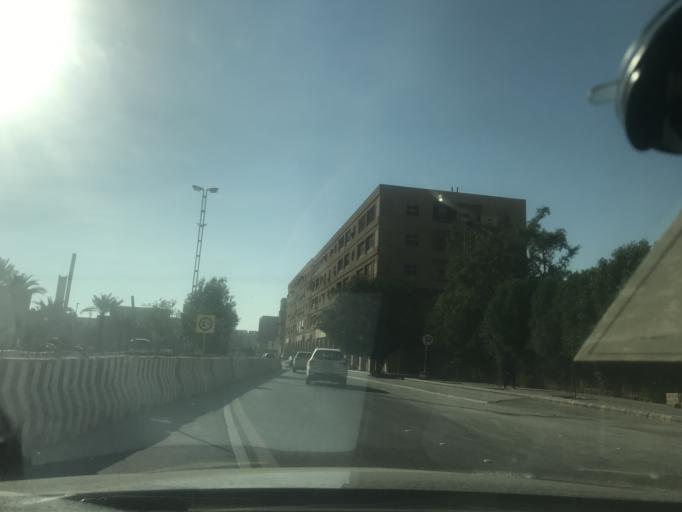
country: SA
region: Ar Riyad
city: Riyadh
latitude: 24.6324
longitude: 46.7146
